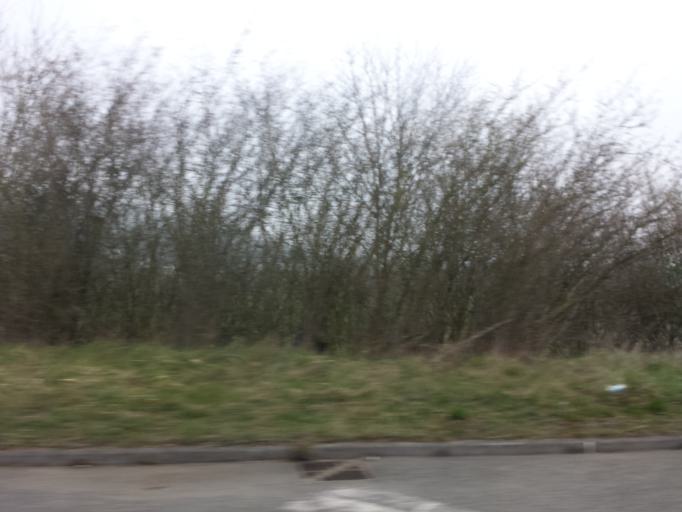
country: GB
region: England
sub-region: Bath and North East Somerset
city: Bath
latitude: 51.3967
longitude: -2.3326
